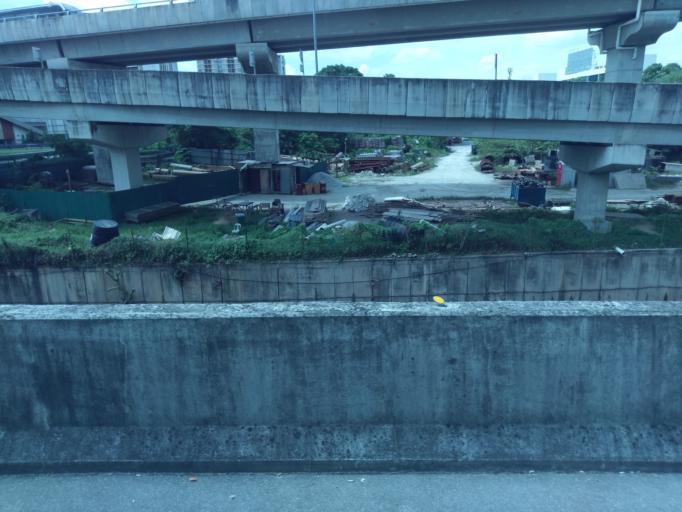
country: MY
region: Selangor
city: Subang Jaya
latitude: 3.0627
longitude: 101.5990
